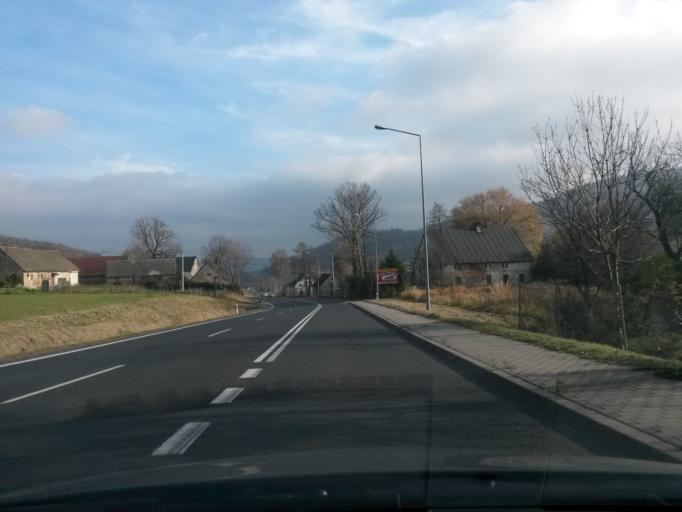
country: PL
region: Lower Silesian Voivodeship
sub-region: Powiat jeleniogorski
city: Janowice Wielkie
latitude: 50.9094
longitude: 15.9359
